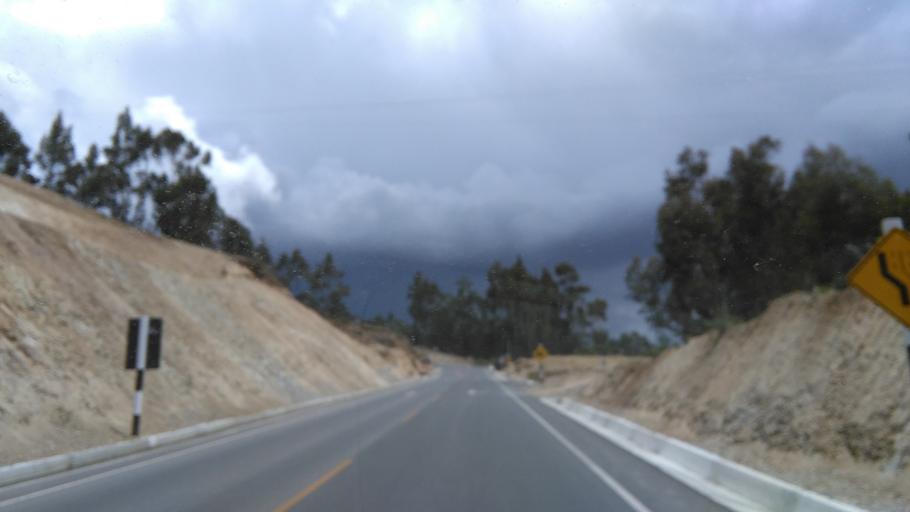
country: PE
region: Apurimac
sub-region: Provincia de Andahuaylas
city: San Jeronimo
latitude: -13.6850
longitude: -73.3577
